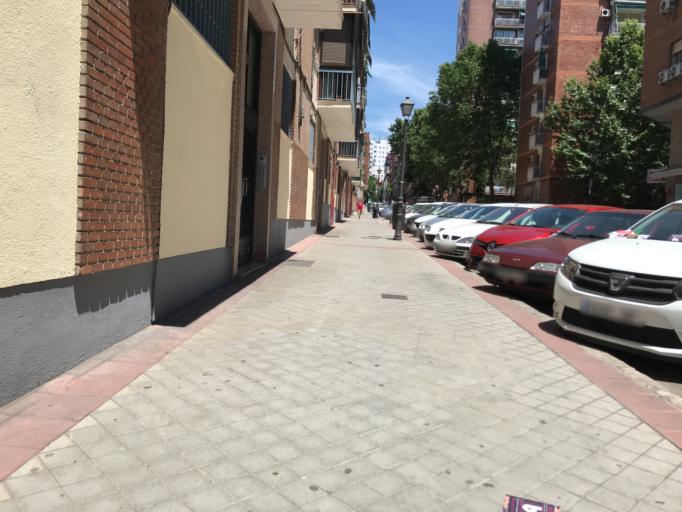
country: ES
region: Madrid
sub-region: Provincia de Madrid
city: Arganzuela
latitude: 40.3970
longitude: -3.6998
